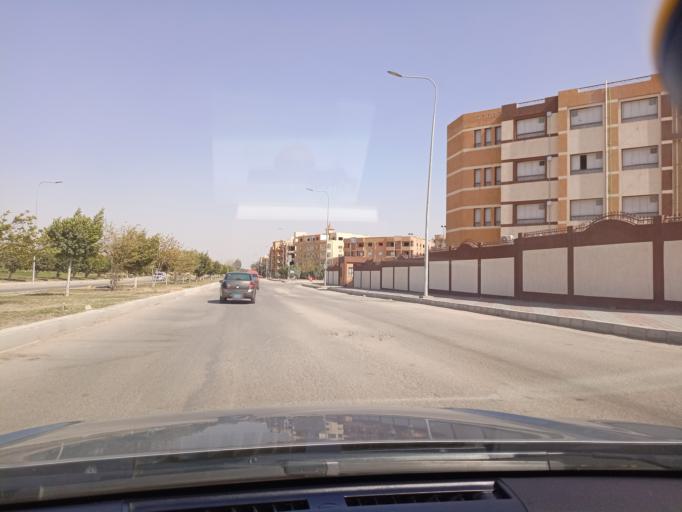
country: EG
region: Muhafazat al Qalyubiyah
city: Al Khankah
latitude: 30.2269
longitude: 31.4484
